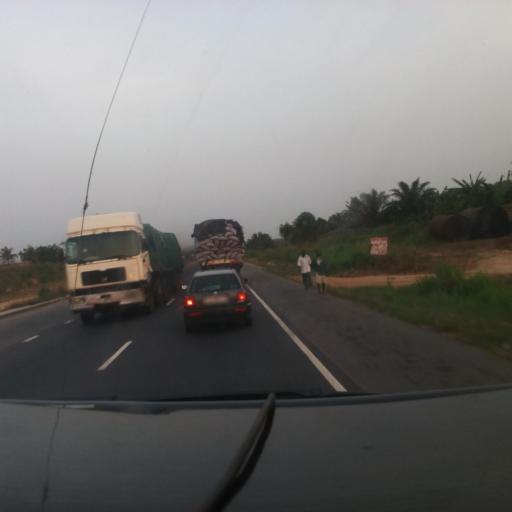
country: GH
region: Eastern
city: Nsawam
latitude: 5.8965
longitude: -0.3863
